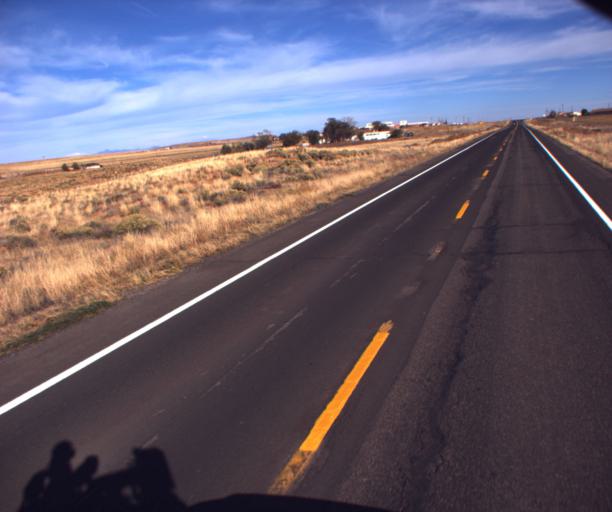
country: US
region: Arizona
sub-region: Apache County
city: Lukachukai
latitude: 36.9601
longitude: -109.3604
